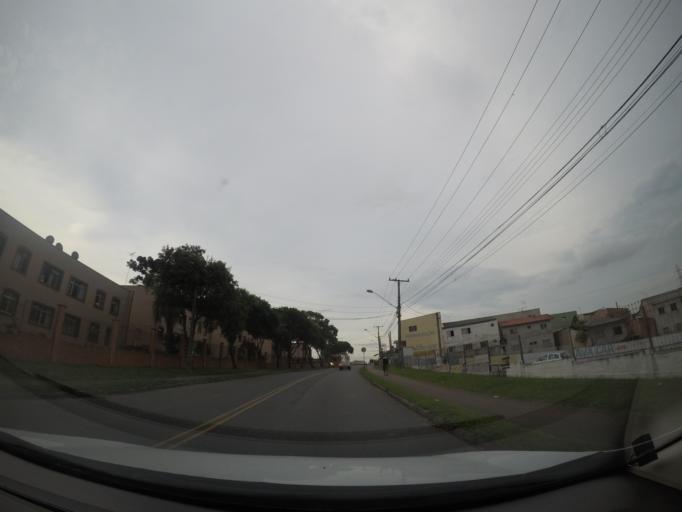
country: BR
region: Parana
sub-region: Sao Jose Dos Pinhais
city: Sao Jose dos Pinhais
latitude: -25.5267
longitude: -49.2394
